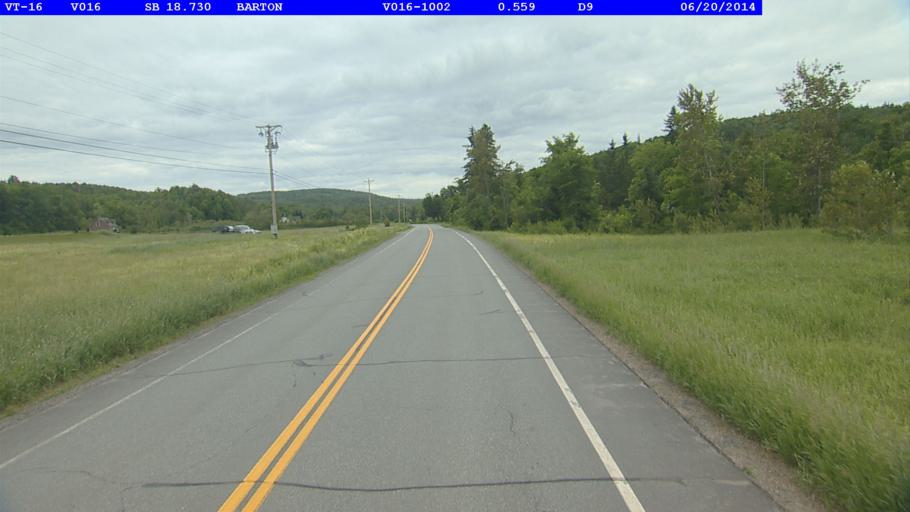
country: US
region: Vermont
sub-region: Orleans County
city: Newport
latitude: 44.7254
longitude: -72.1851
